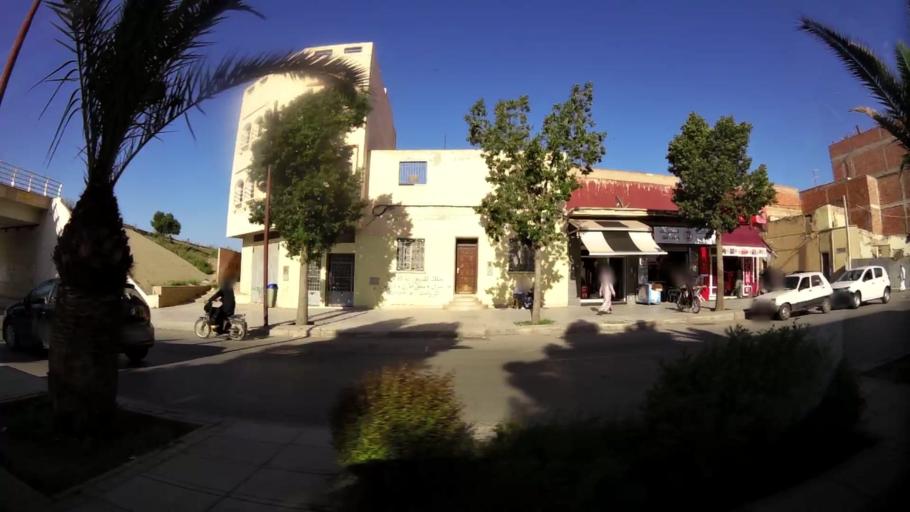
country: MA
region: Oriental
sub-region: Oujda-Angad
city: Oujda
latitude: 34.6962
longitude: -1.9189
